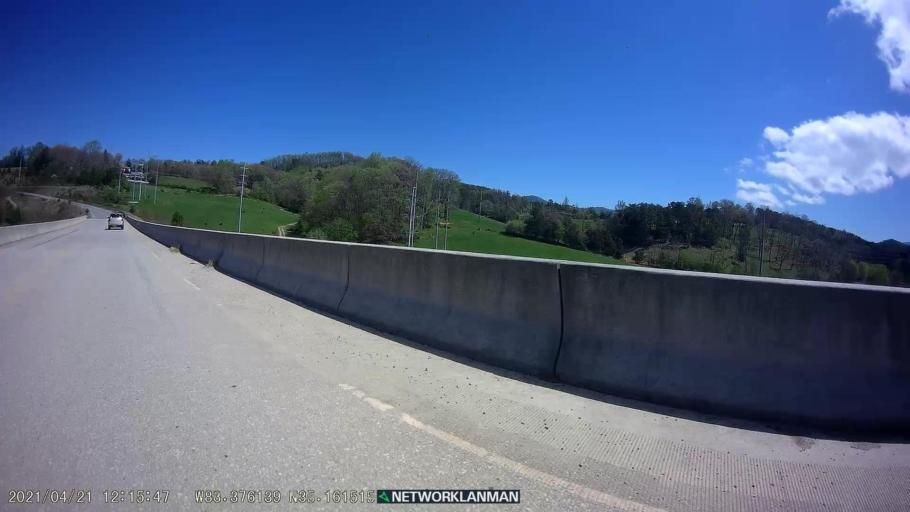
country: US
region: North Carolina
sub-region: Macon County
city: Franklin
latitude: 35.1617
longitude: -83.3758
